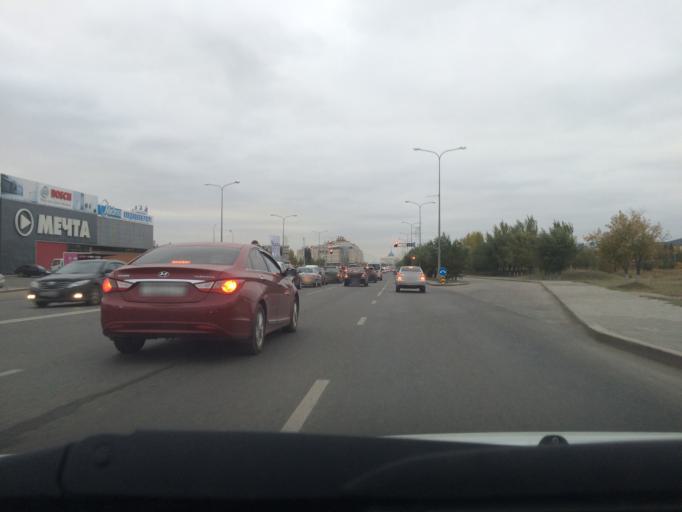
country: KZ
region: Astana Qalasy
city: Astana
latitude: 51.1497
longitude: 71.4445
